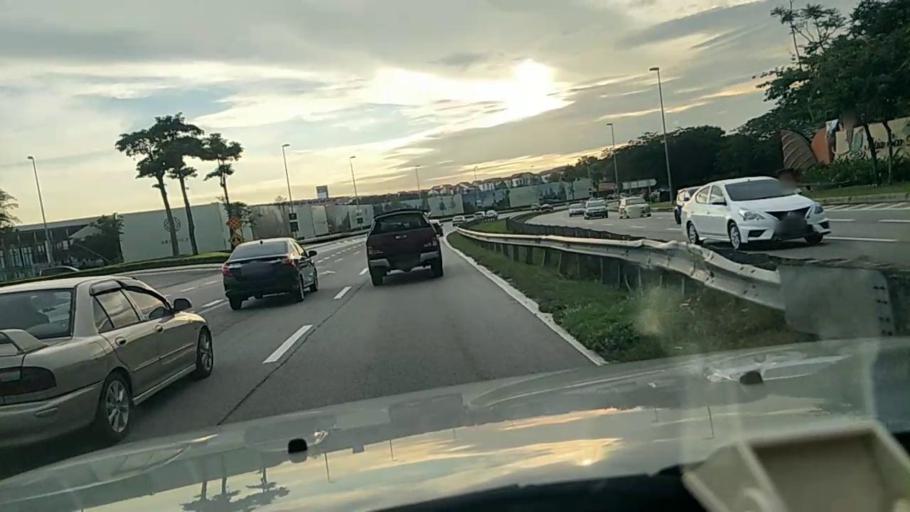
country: MY
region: Selangor
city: Shah Alam
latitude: 3.0995
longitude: 101.4775
